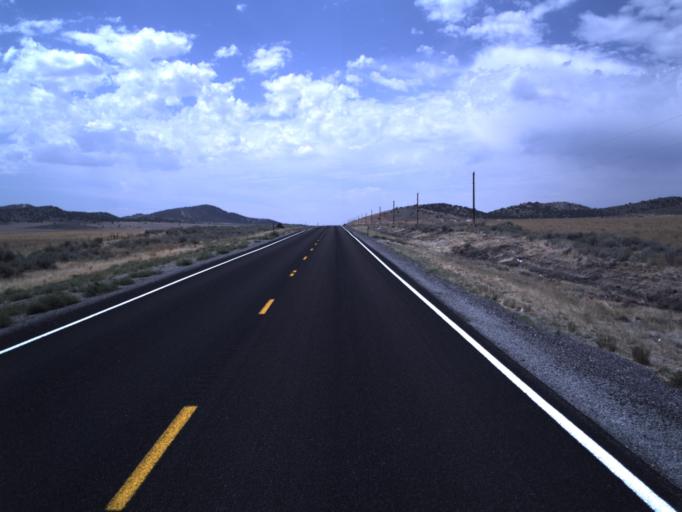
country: US
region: Utah
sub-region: Utah County
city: Eagle Mountain
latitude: 40.2478
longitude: -112.1290
